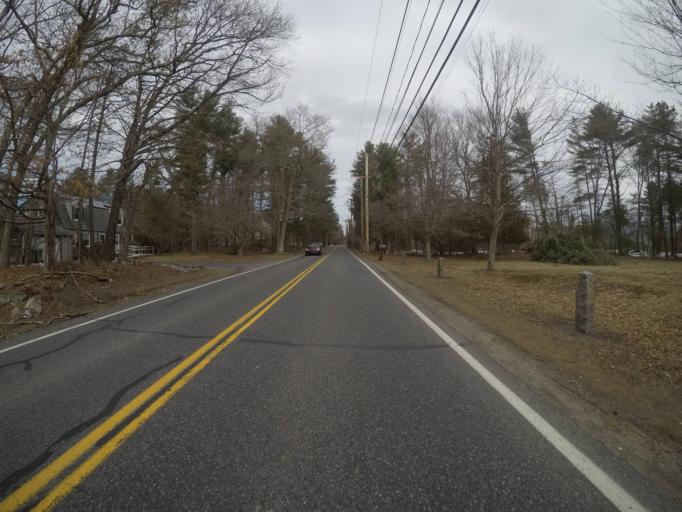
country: US
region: Massachusetts
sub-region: Bristol County
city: Easton
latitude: 42.0558
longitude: -71.1307
